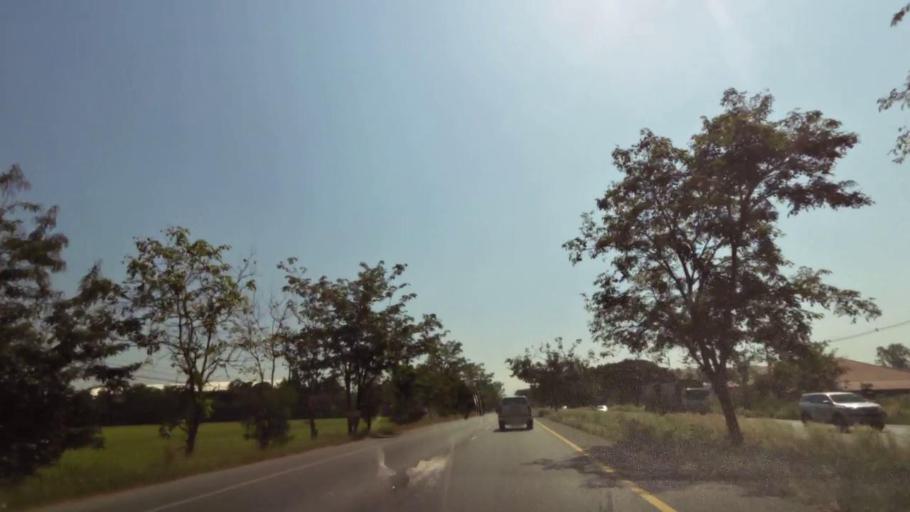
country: TH
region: Nakhon Sawan
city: Kao Liao
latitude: 15.8546
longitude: 100.1170
